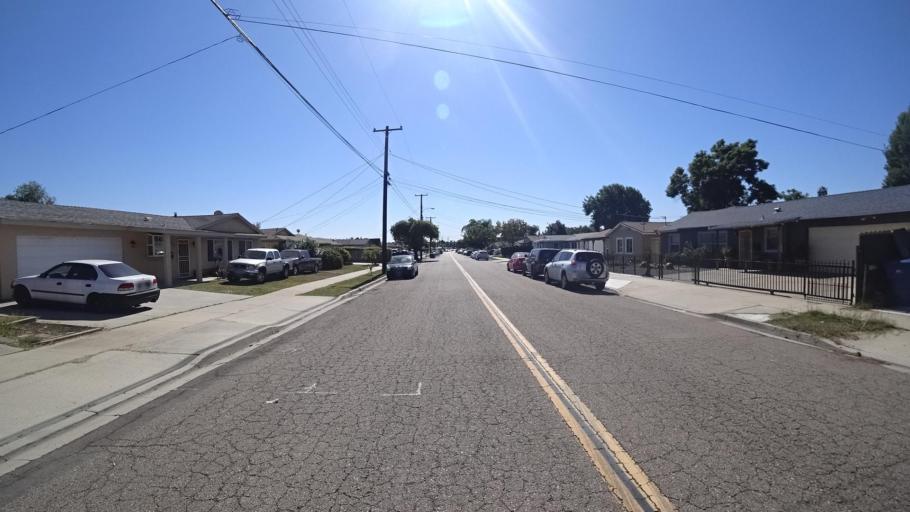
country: US
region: California
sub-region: San Diego County
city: La Presa
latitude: 32.7118
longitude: -117.0153
